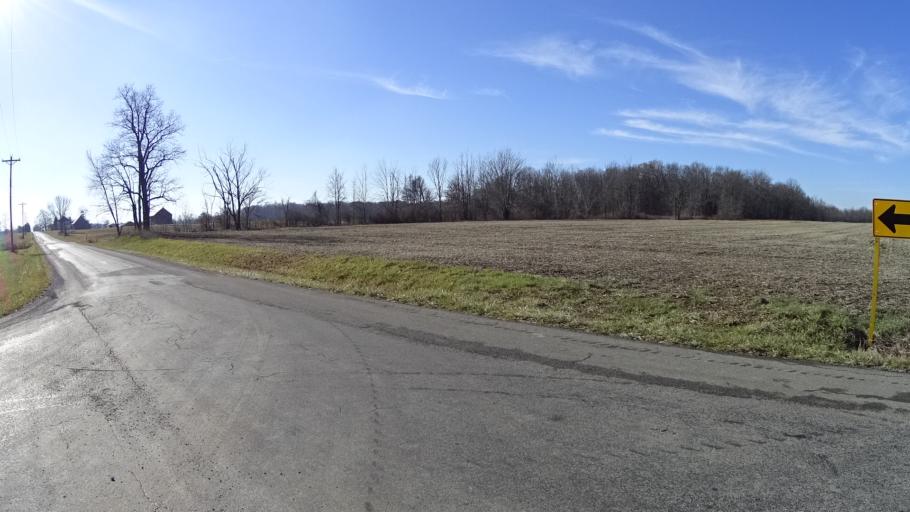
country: US
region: Ohio
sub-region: Huron County
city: New London
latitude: 41.1296
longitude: -82.3306
